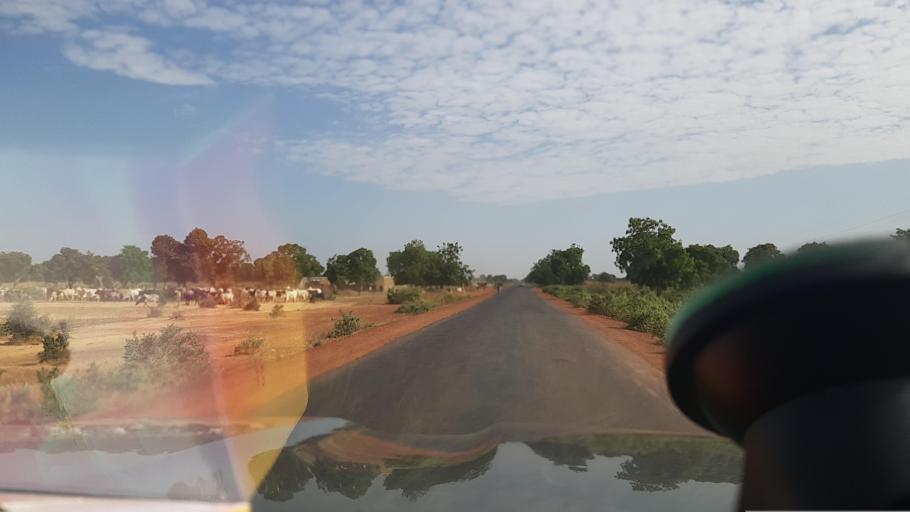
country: ML
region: Segou
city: Segou
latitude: 13.5042
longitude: -6.1480
